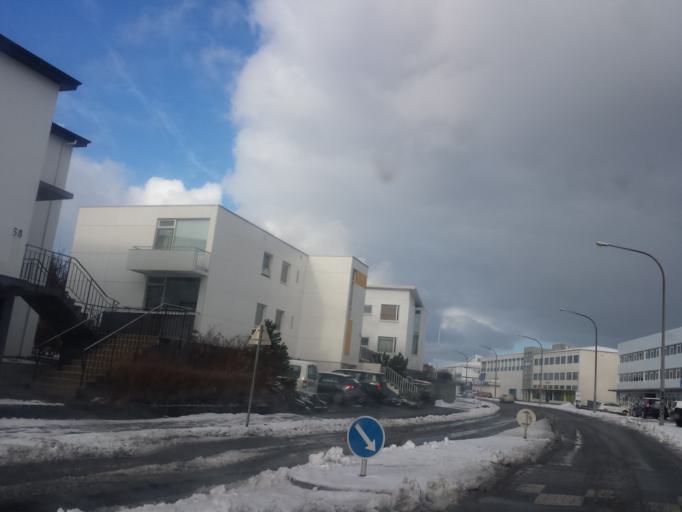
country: IS
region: Capital Region
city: Reykjavik
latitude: 64.1392
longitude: -21.8969
